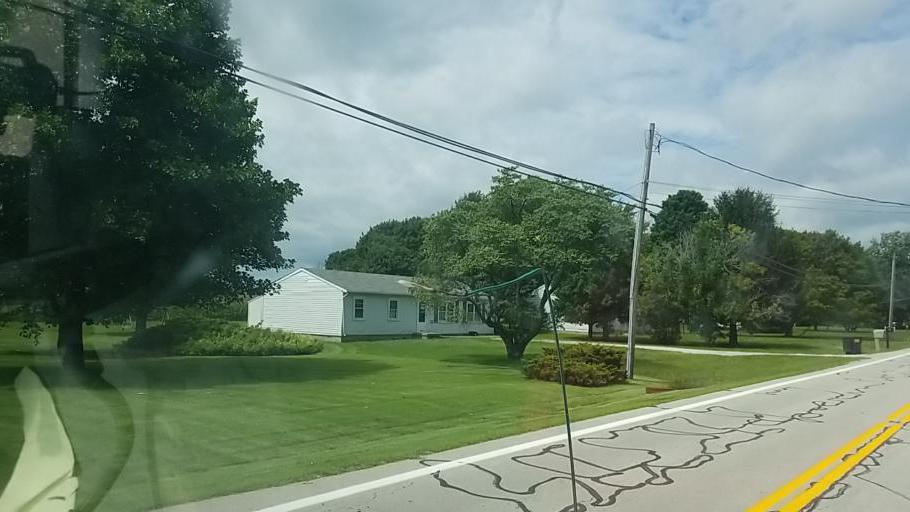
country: US
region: Ohio
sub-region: Fayette County
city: Jeffersonville
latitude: 39.6581
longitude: -83.5676
